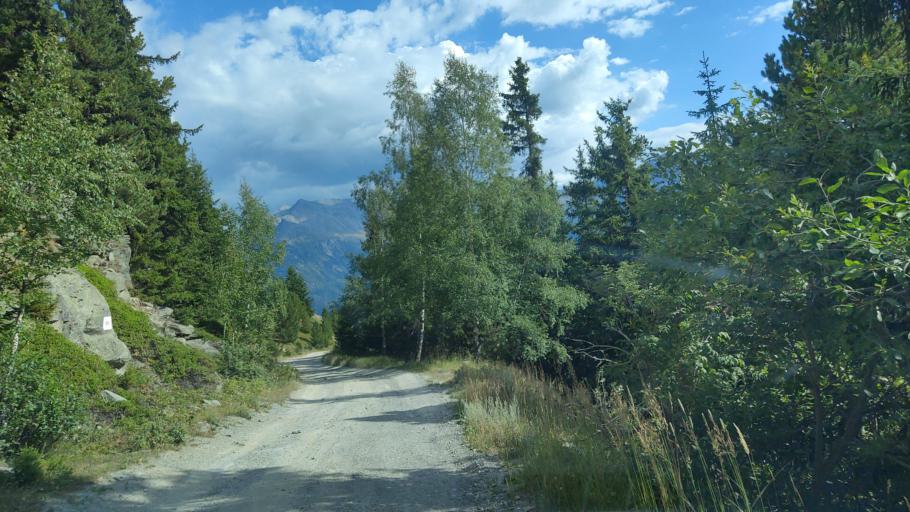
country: FR
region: Rhone-Alpes
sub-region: Departement de la Savoie
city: Val Thorens
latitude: 45.2291
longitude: 6.5607
